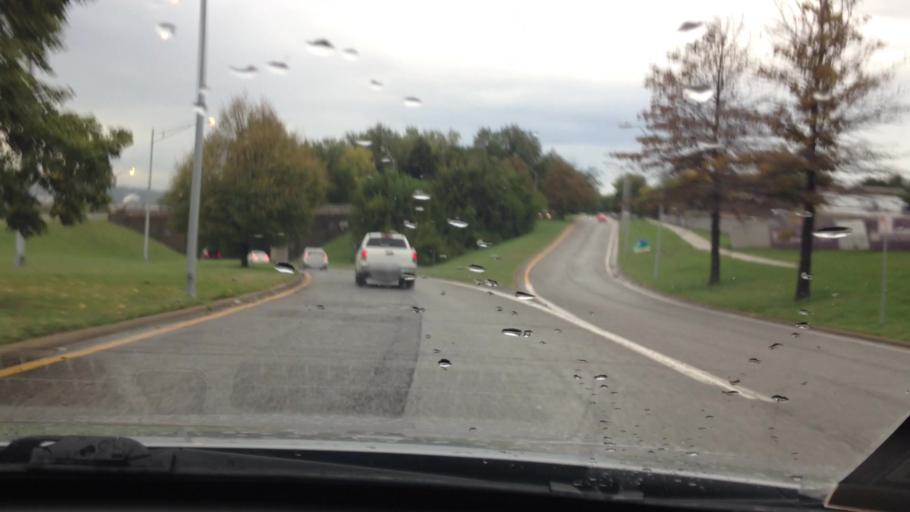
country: US
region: Missouri
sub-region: Jackson County
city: Kansas City
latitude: 39.1070
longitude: -94.5635
